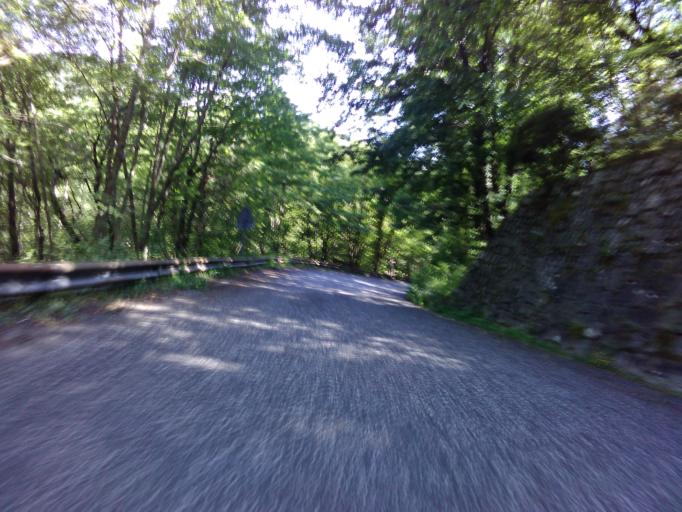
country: IT
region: Tuscany
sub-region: Provincia di Massa-Carrara
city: Comano
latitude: 44.3155
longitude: 10.0899
